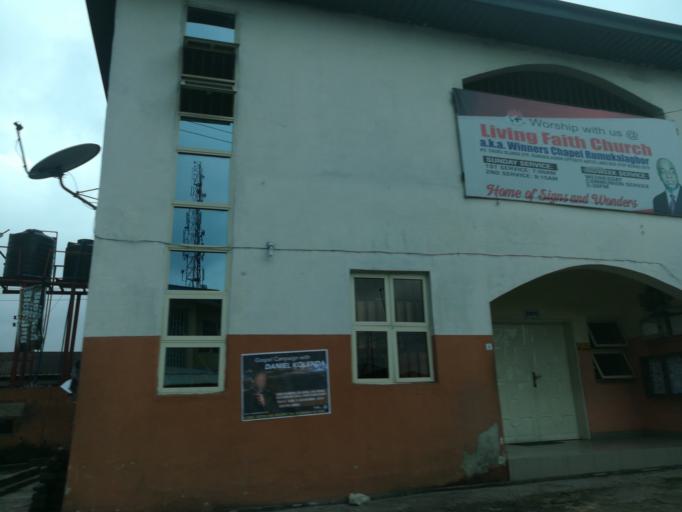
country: NG
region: Rivers
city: Port Harcourt
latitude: 4.8163
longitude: 7.0107
